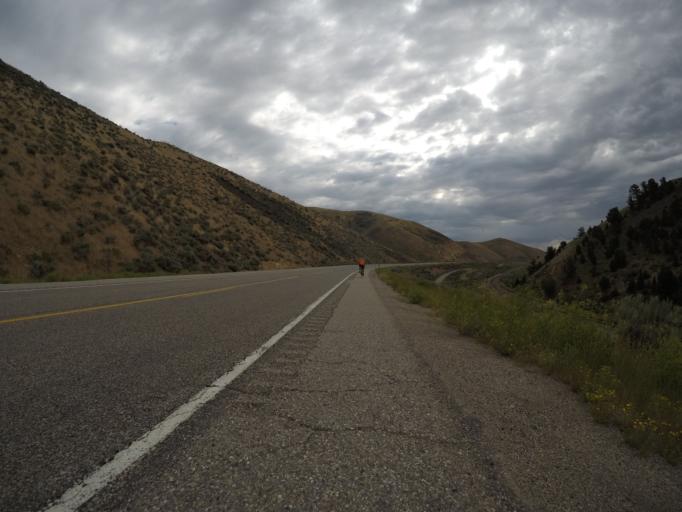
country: US
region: Wyoming
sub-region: Lincoln County
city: Kemmerer
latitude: 41.8247
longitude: -110.8539
